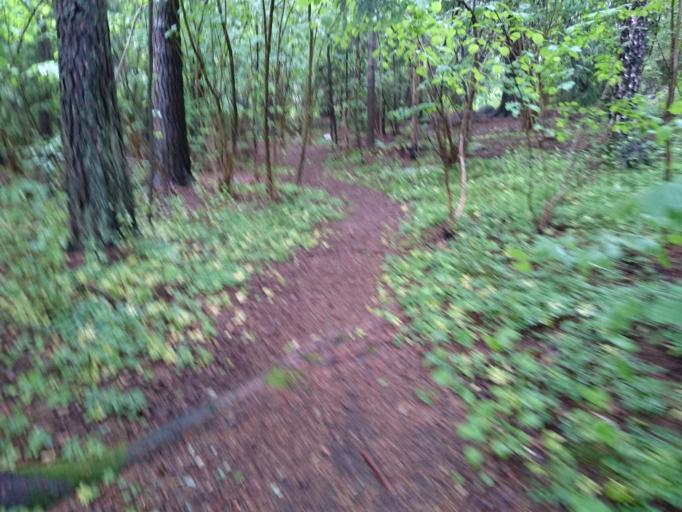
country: SE
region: Stockholm
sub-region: Huddinge Kommun
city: Segeltorp
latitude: 59.2702
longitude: 17.9287
